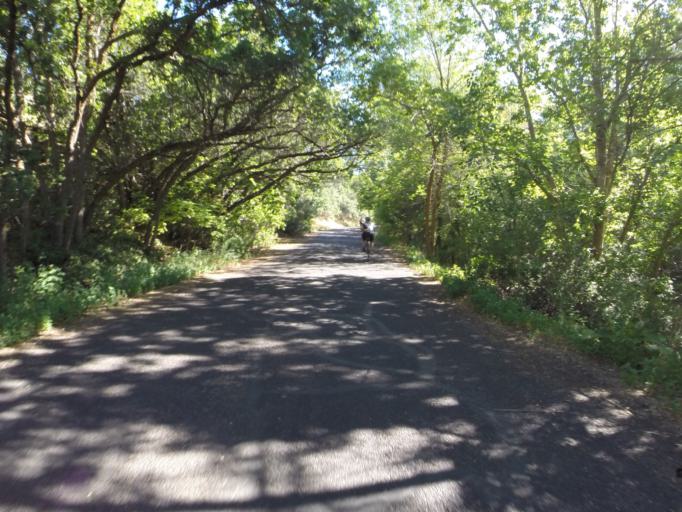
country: US
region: Utah
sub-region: Salt Lake County
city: Salt Lake City
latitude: 40.7884
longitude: -111.8807
